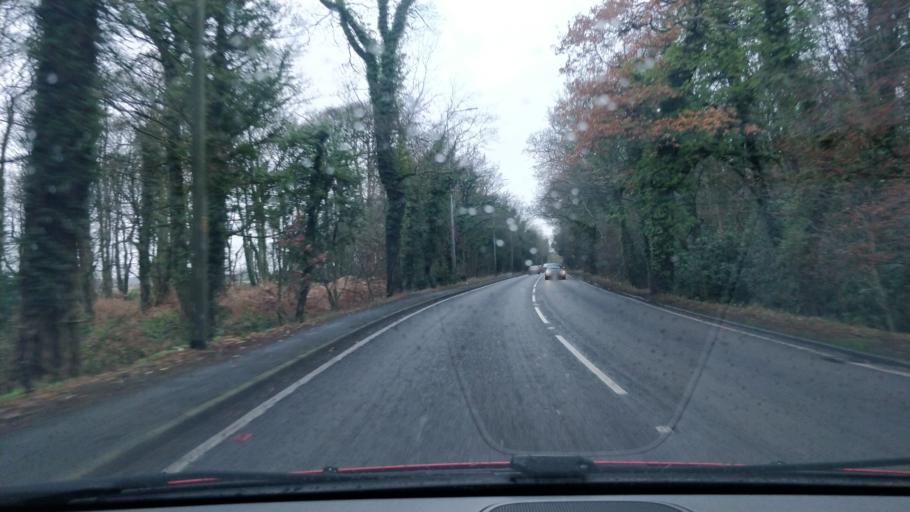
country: GB
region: England
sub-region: Sefton
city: Ince Blundell
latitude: 53.5175
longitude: -3.0222
